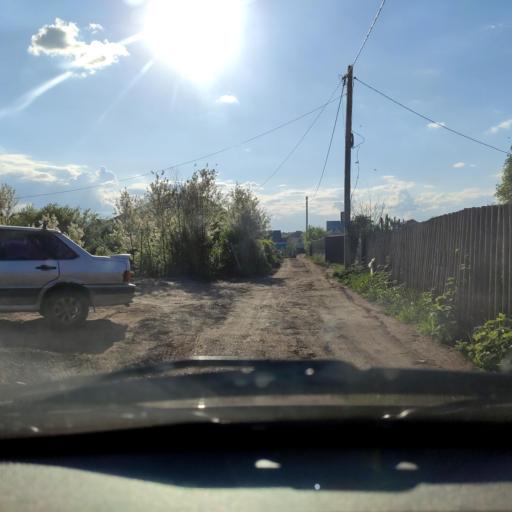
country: RU
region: Bashkortostan
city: Mikhaylovka
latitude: 54.8344
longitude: 55.9506
